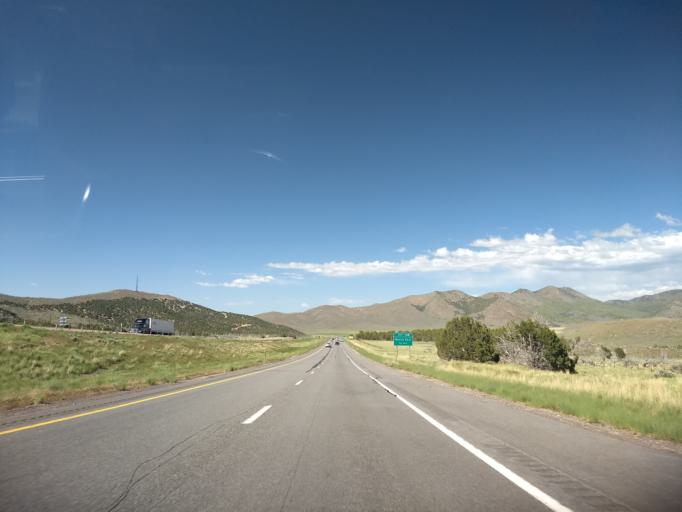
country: US
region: Utah
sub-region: Beaver County
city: Beaver
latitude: 38.6484
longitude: -112.6014
